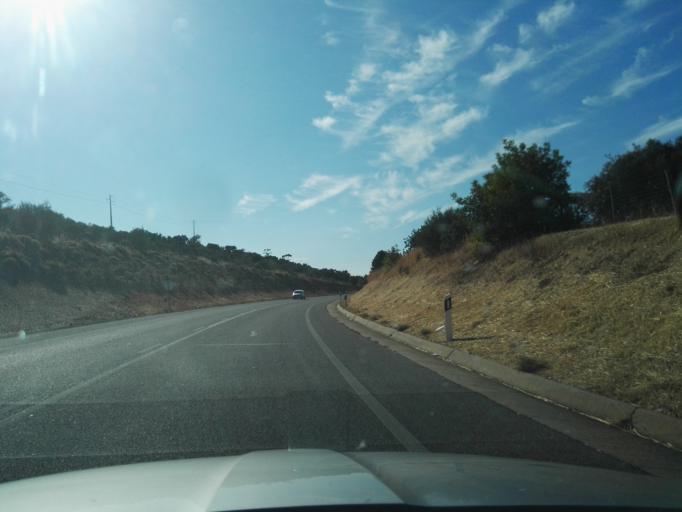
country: PT
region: Faro
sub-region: Sao Bras de Alportel
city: Sao Bras de Alportel
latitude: 37.1480
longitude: -7.9197
